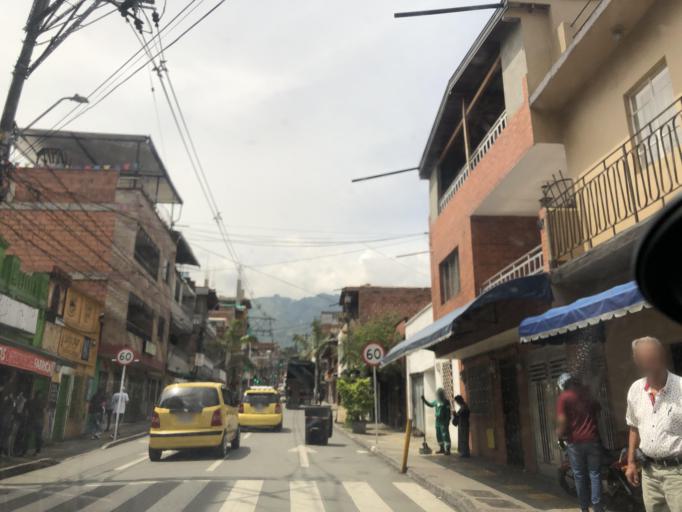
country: CO
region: Antioquia
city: Bello
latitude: 6.3372
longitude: -75.5563
